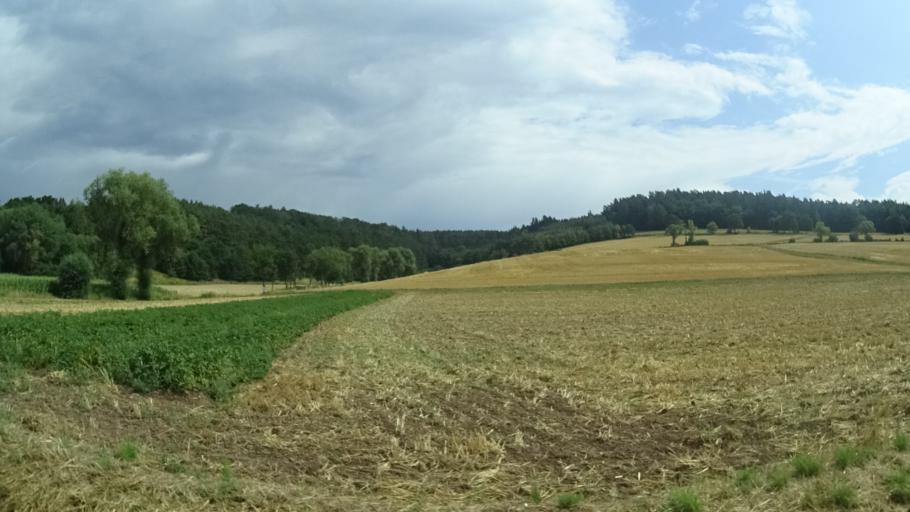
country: DE
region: Hesse
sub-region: Regierungsbezirk Kassel
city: Niederaula
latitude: 50.7966
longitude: 9.6255
